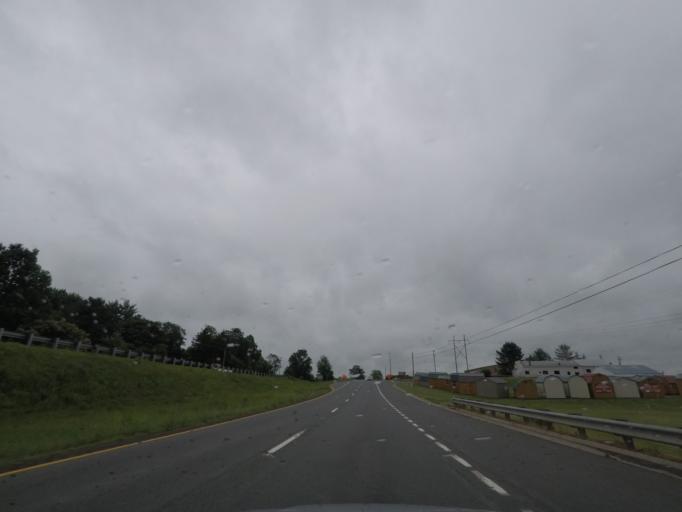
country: US
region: Virginia
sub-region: Orange County
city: Orange
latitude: 38.2205
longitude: -78.1256
